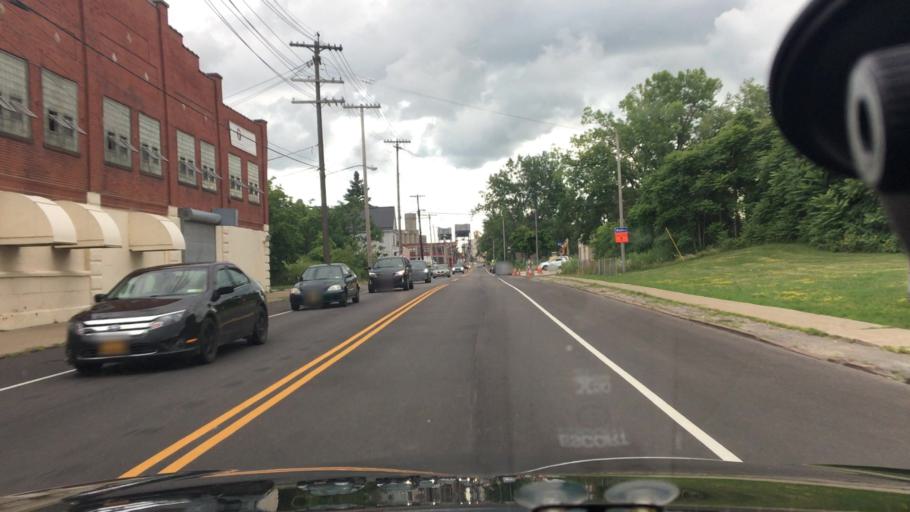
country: US
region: New York
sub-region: Erie County
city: Buffalo
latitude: 42.8711
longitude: -78.8648
